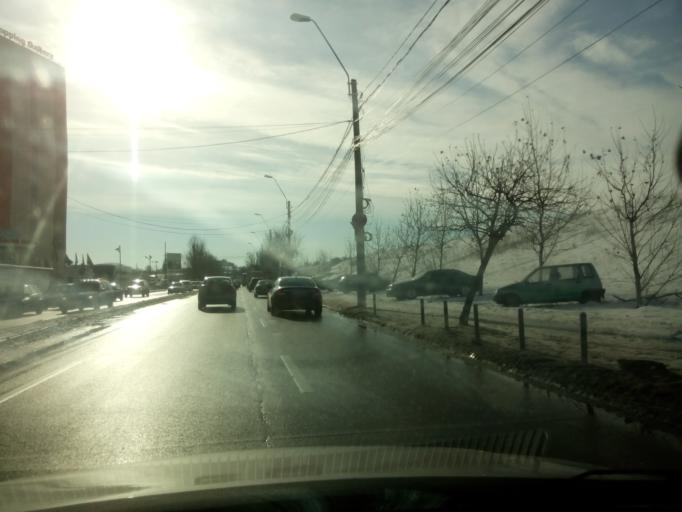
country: RO
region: Ilfov
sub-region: Comuna Popesti-Leordeni
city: Popesti-Leordeni
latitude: 44.3995
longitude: 26.1427
